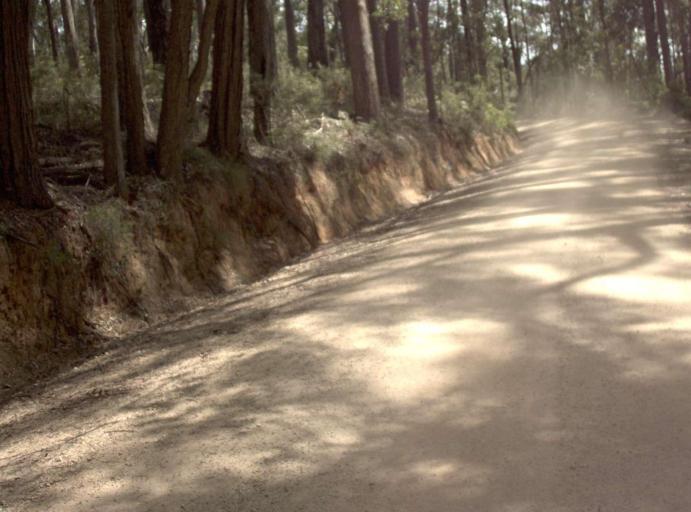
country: AU
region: Victoria
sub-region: East Gippsland
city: Lakes Entrance
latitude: -37.5877
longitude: 148.7253
